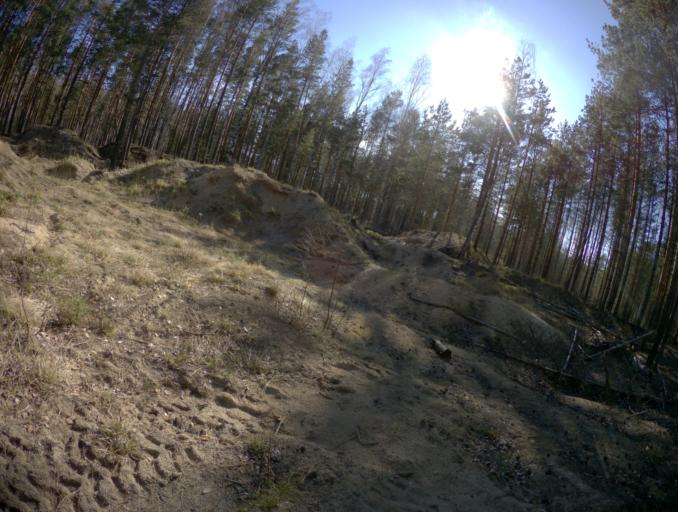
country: RU
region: Vladimir
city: Ivanishchi
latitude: 55.6972
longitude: 40.4265
